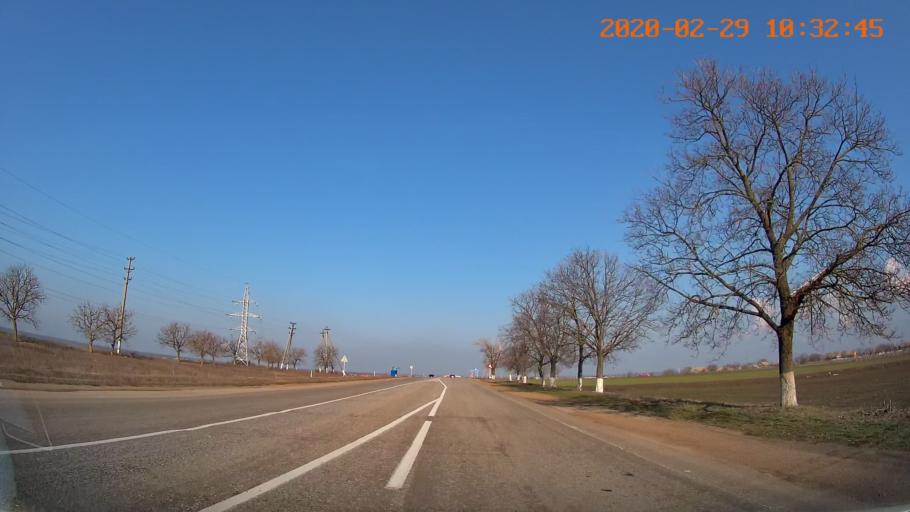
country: UA
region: Odessa
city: Velykoploske
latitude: 46.9648
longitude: 29.5514
